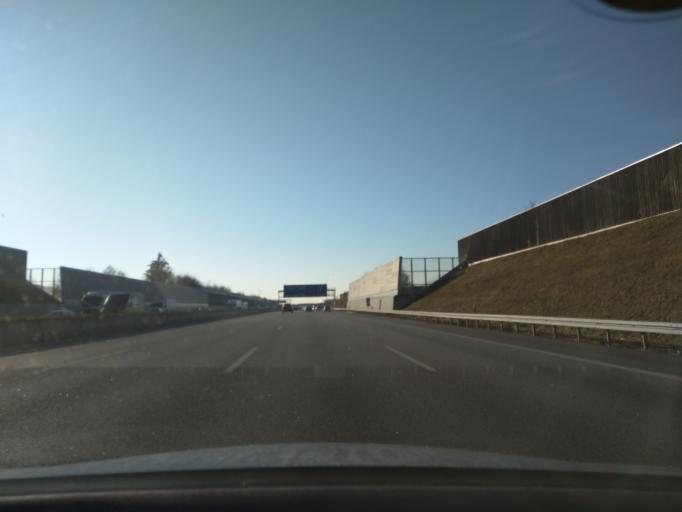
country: DE
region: Bavaria
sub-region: Upper Bavaria
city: Garching bei Munchen
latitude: 48.2512
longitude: 11.6443
